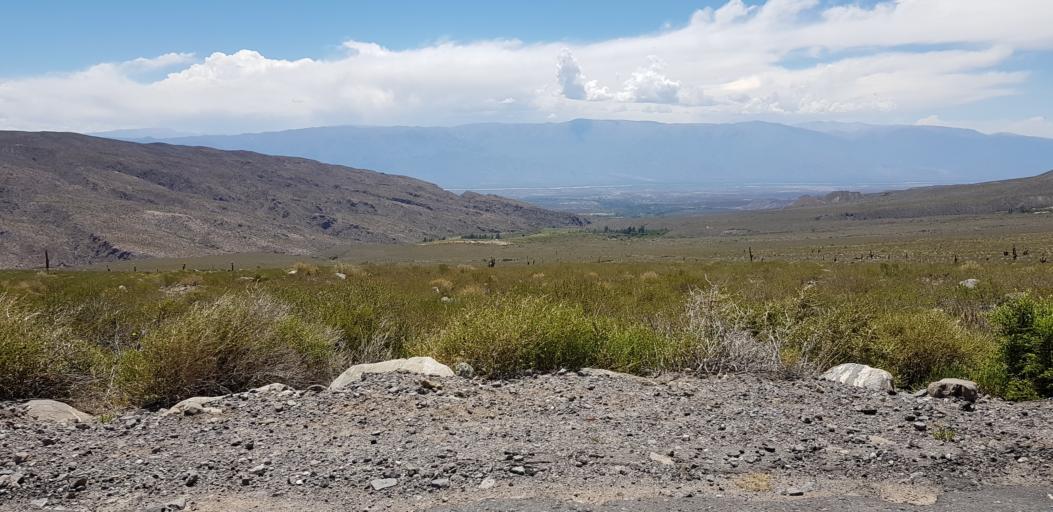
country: AR
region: Tucuman
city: Tafi del Valle
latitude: -26.6667
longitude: -65.8178
